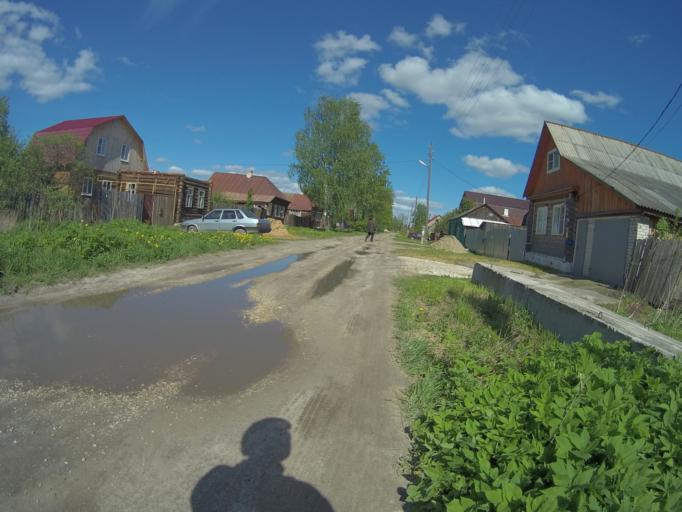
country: RU
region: Vladimir
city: Sudogda
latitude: 55.9536
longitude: 40.8519
